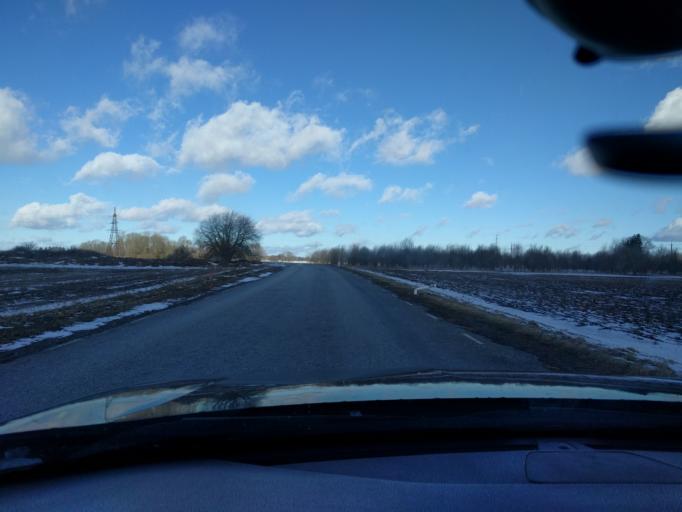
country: EE
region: Harju
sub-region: Raasiku vald
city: Raasiku
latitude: 59.3425
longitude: 25.1516
